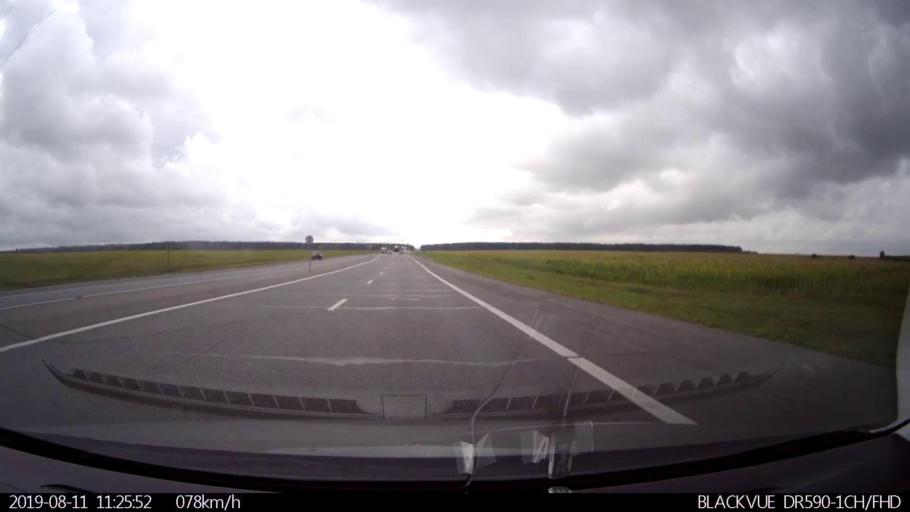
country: RU
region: Ulyanovsk
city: Krasnyy Gulyay
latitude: 54.1122
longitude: 48.2368
